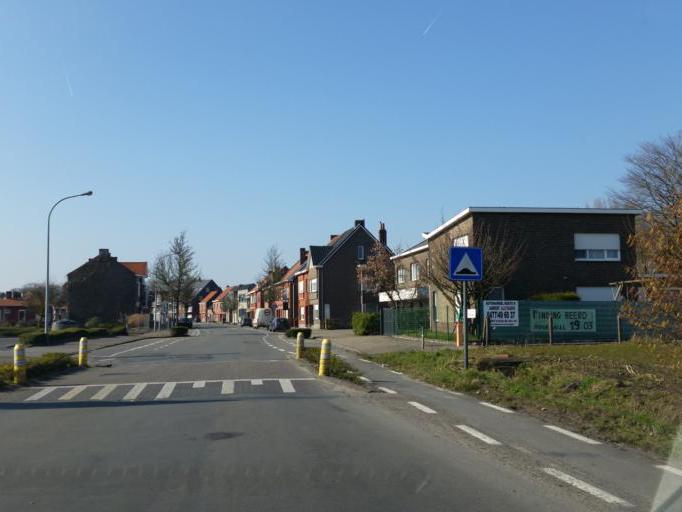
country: BE
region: Flanders
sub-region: Provincie Oost-Vlaanderen
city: Assenede
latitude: 51.1781
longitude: 3.7553
